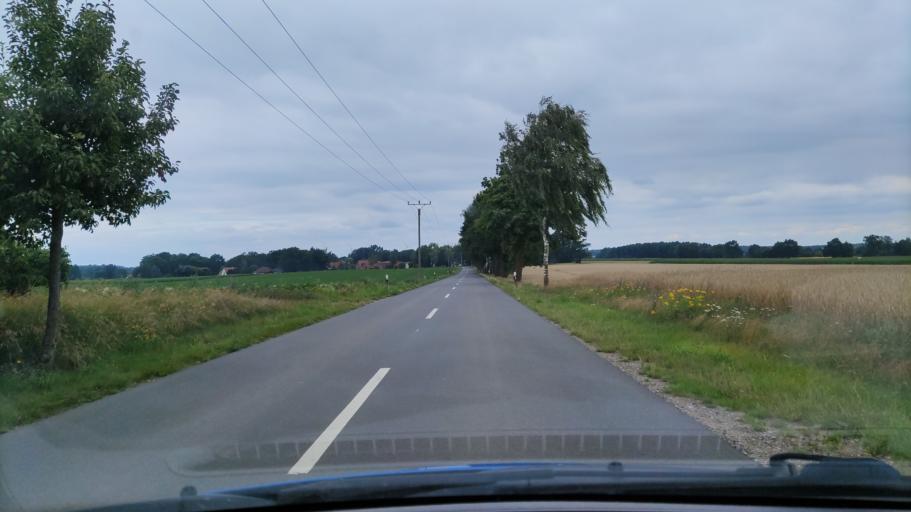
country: DE
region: Lower Saxony
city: Rosche
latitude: 53.0060
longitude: 10.7580
